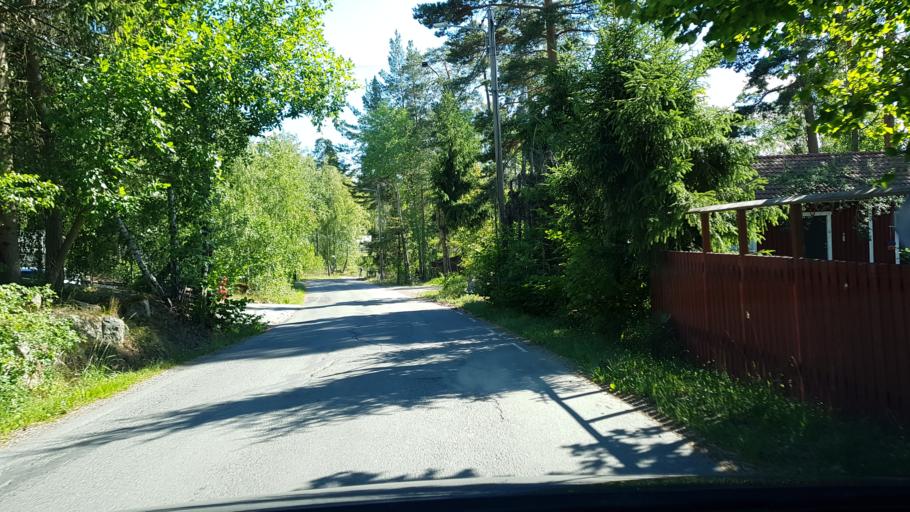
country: SE
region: Stockholm
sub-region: Upplands-Bro Kommun
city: Kungsaengen
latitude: 59.4795
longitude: 17.8001
